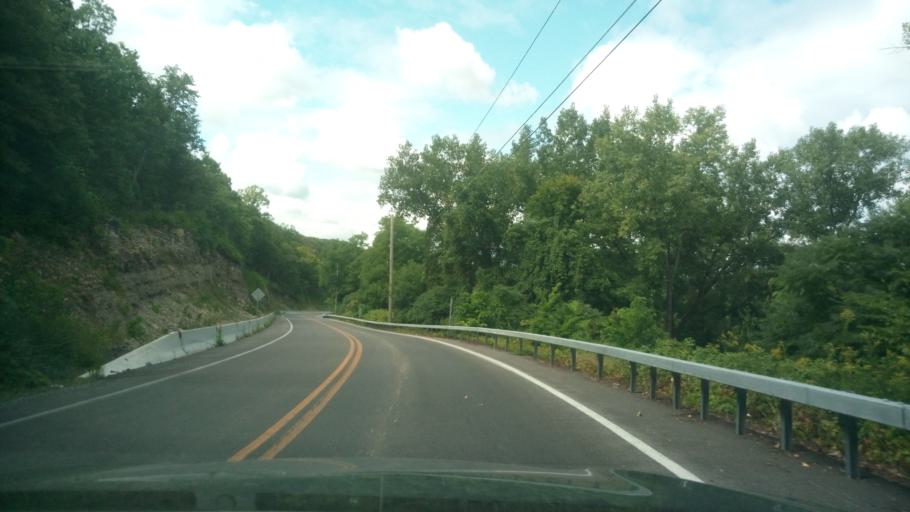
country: US
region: New York
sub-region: Onondaga County
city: East Syracuse
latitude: 43.0050
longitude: -76.0852
